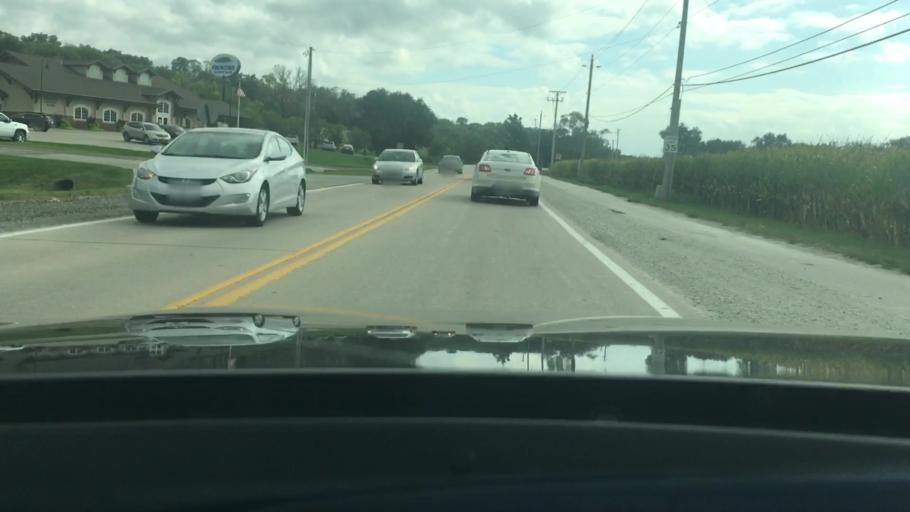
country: US
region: Iowa
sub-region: Pottawattamie County
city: Council Bluffs
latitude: 41.2497
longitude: -95.8144
